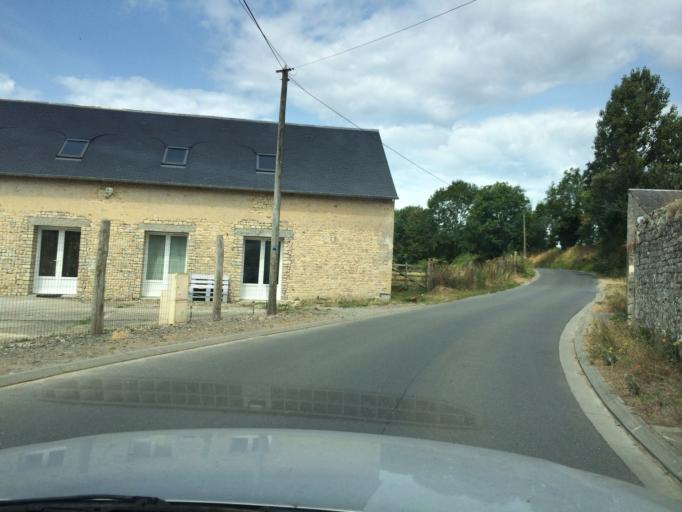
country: FR
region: Lower Normandy
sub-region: Departement du Calvados
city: Bayeux
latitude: 49.2861
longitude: -0.7359
